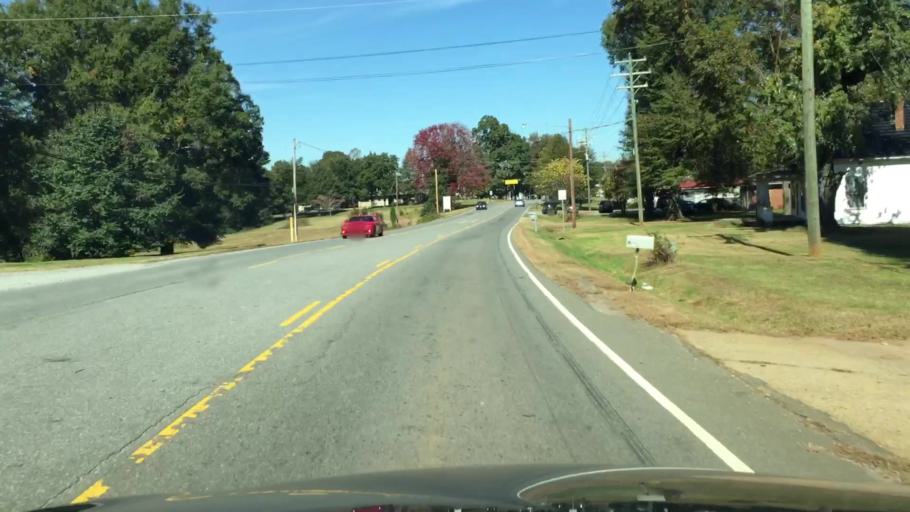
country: US
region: North Carolina
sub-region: Rockingham County
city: Reidsville
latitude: 36.3330
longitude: -79.6517
